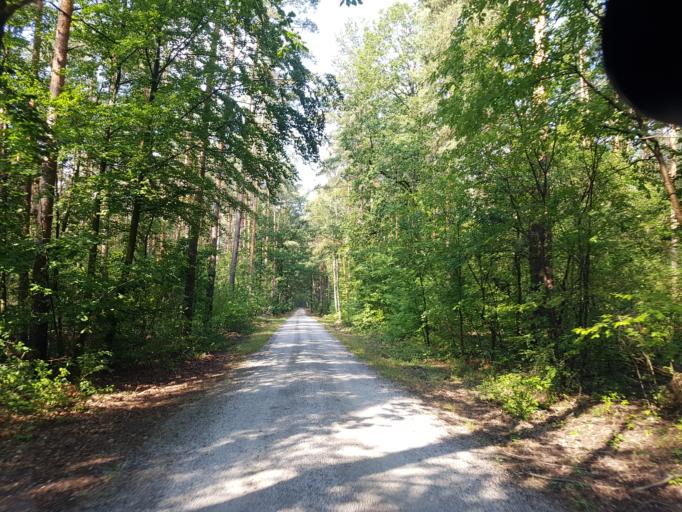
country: DE
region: Brandenburg
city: Hohenleipisch
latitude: 51.5142
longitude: 13.5734
